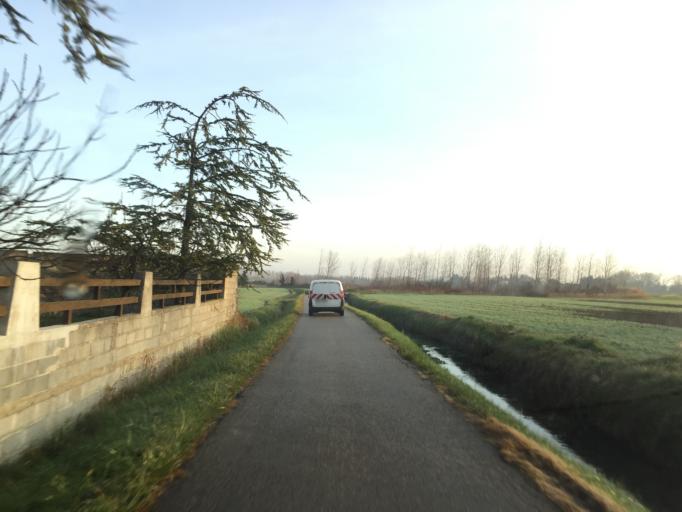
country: FR
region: Provence-Alpes-Cote d'Azur
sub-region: Departement du Vaucluse
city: Caderousse
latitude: 44.1134
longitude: 4.7597
